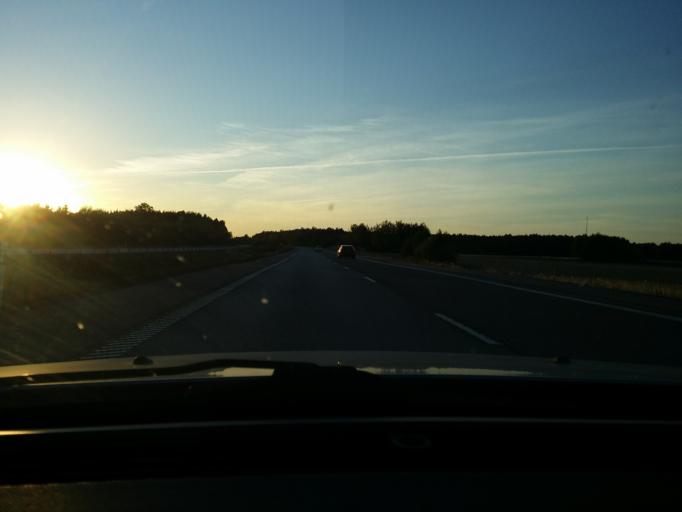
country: SE
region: Uppsala
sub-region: Habo Kommun
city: Balsta
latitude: 59.6035
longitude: 17.4345
